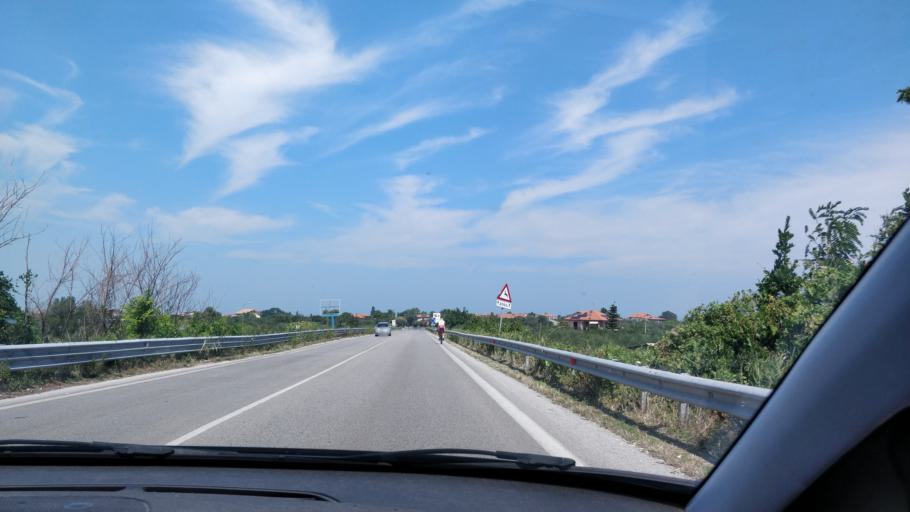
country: IT
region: Abruzzo
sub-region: Provincia di Chieti
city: Ortona
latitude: 42.3645
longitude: 14.3824
